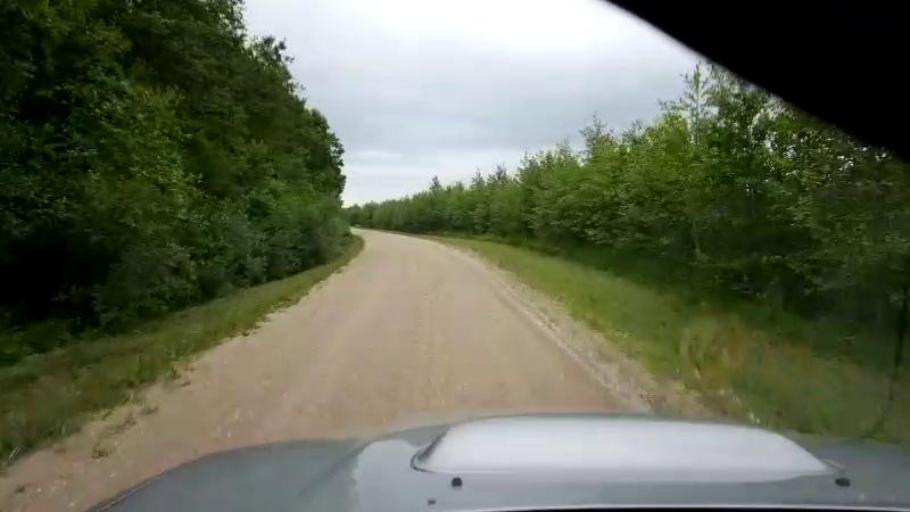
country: EE
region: Paernumaa
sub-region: Halinga vald
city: Parnu-Jaagupi
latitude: 58.5546
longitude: 24.5618
